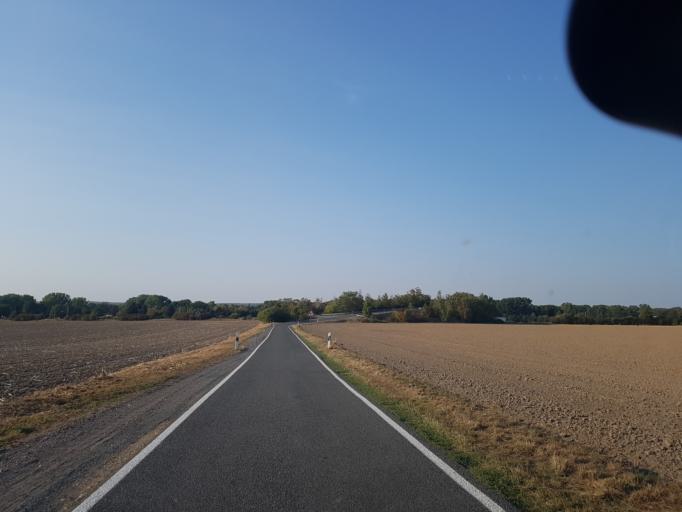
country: DE
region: Saxony
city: Stauchitz
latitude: 51.3015
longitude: 13.1879
